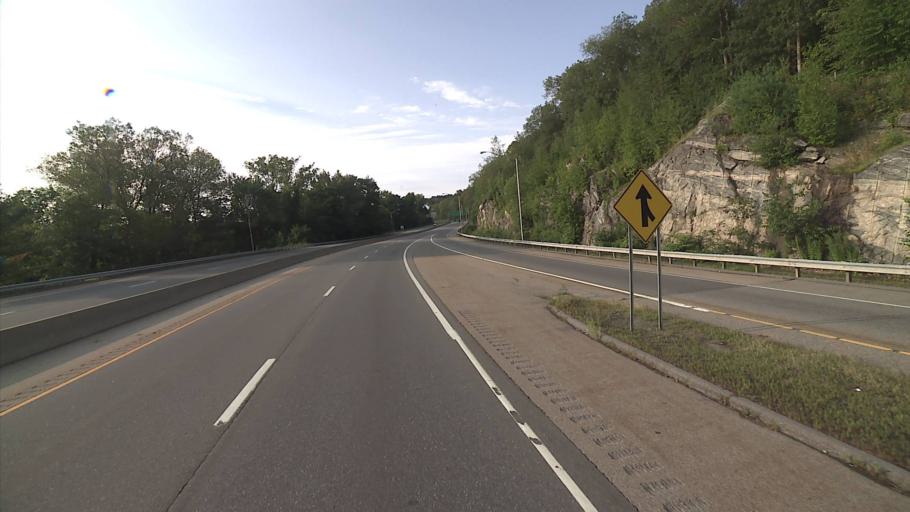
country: US
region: Connecticut
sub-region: New London County
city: Norwich
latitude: 41.5550
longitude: -72.1178
